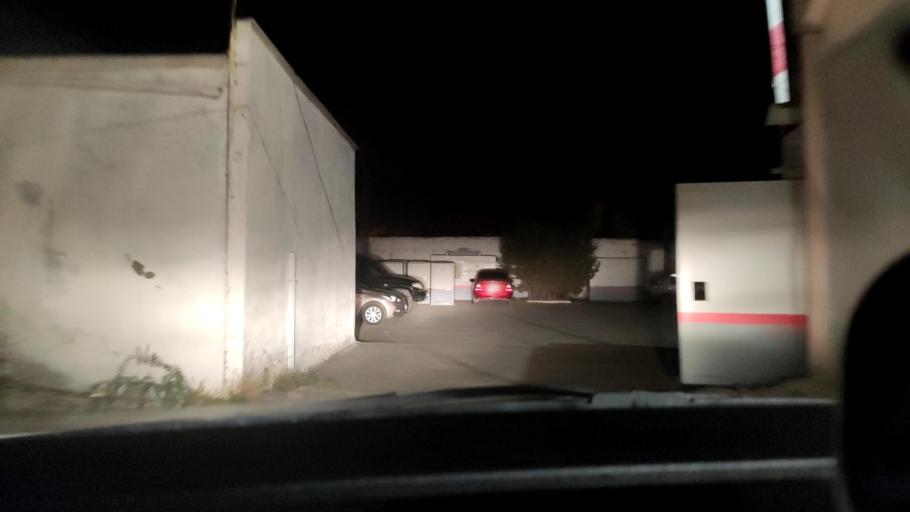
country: RU
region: Voronezj
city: Voronezh
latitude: 51.6767
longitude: 39.1914
